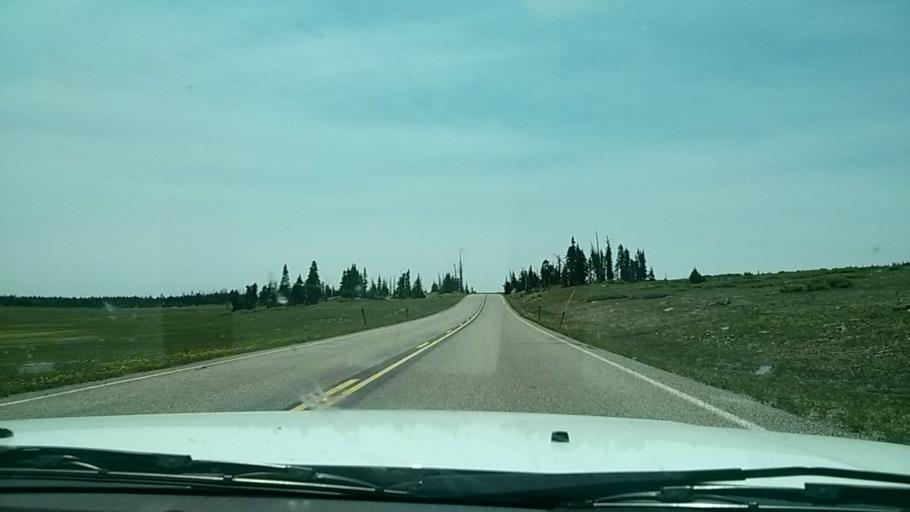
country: US
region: Utah
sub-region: Iron County
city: Cedar City
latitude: 37.6032
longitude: -112.8507
